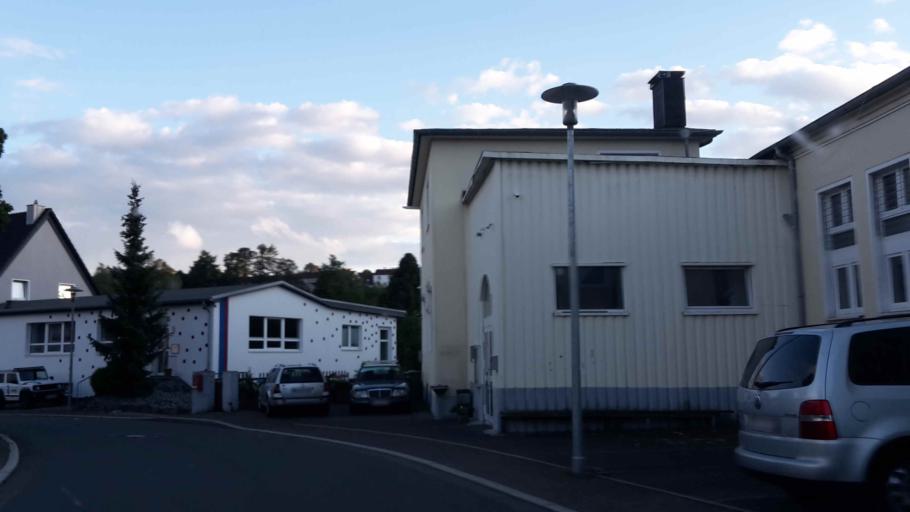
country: DE
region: North Rhine-Westphalia
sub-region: Regierungsbezirk Arnsberg
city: Luedenscheid
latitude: 51.2266
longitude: 7.6378
